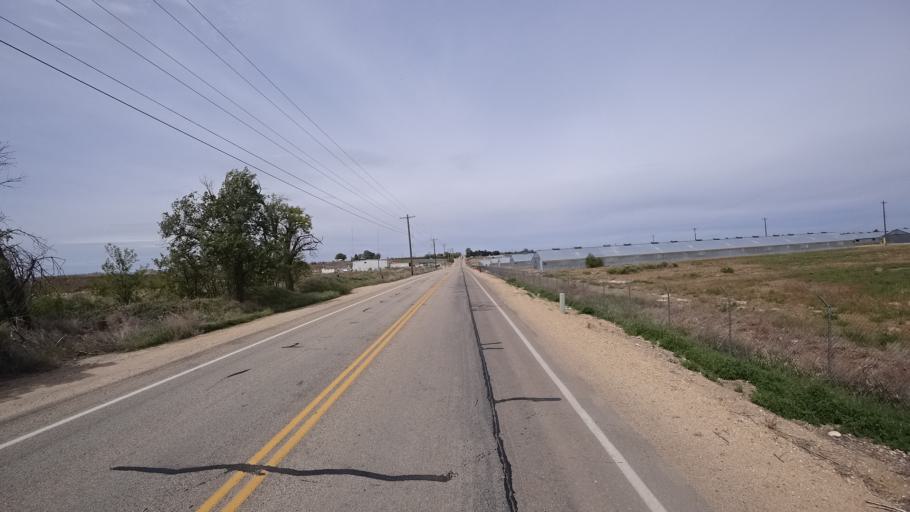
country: US
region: Idaho
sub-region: Ada County
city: Meridian
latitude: 43.5611
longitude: -116.3864
